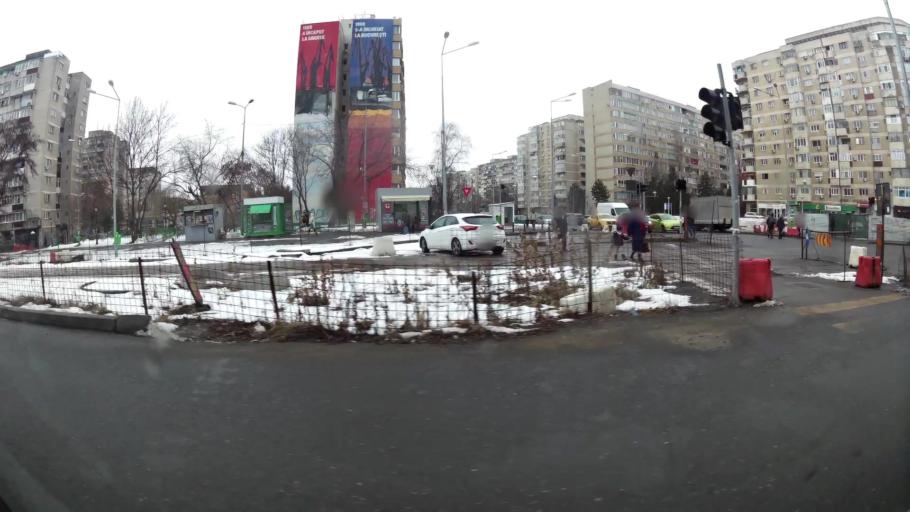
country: RO
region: Ilfov
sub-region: Comuna Chiajna
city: Rosu
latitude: 44.4207
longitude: 26.0205
